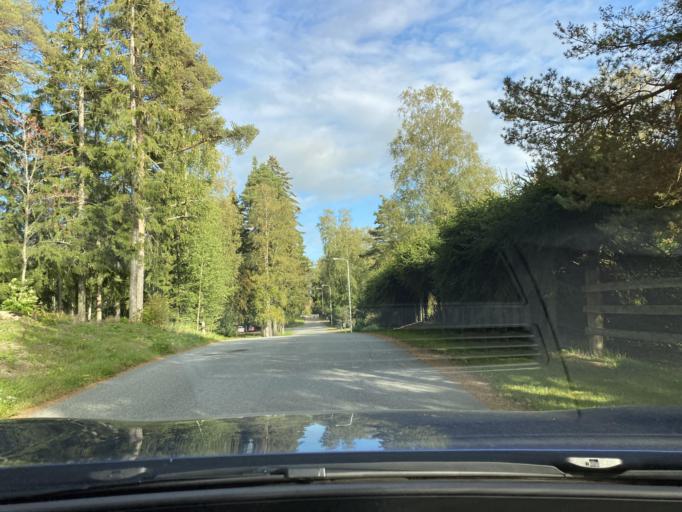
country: FI
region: Pirkanmaa
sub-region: Lounais-Pirkanmaa
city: Vammala
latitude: 61.3354
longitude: 22.9237
